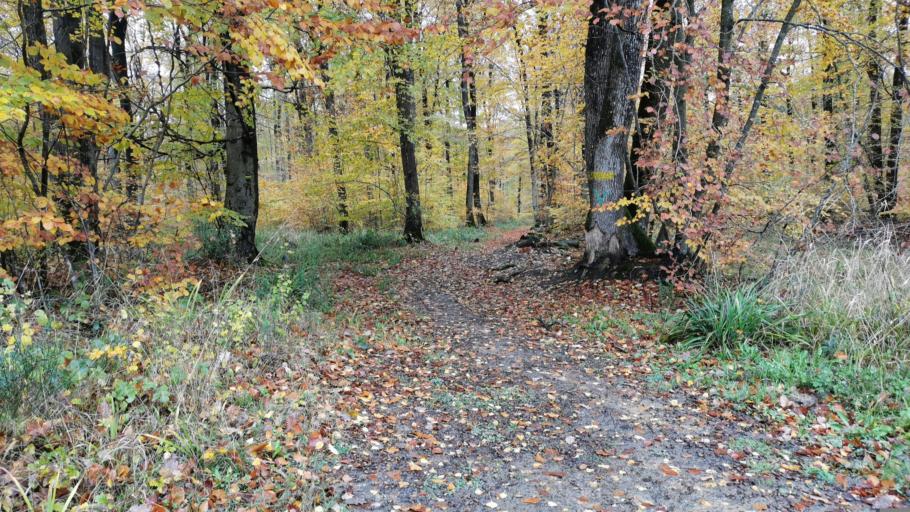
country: FR
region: Picardie
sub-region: Departement de l'Aisne
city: Saint-Gobain
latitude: 49.5859
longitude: 3.3708
